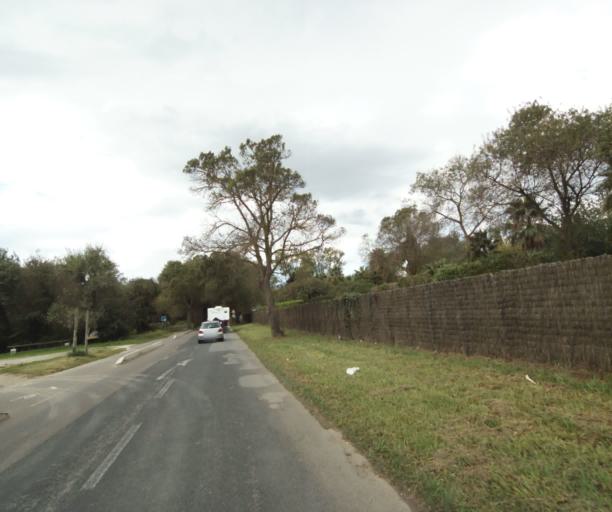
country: FR
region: Languedoc-Roussillon
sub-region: Departement des Pyrenees-Orientales
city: Argelers
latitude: 42.5630
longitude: 3.0340
